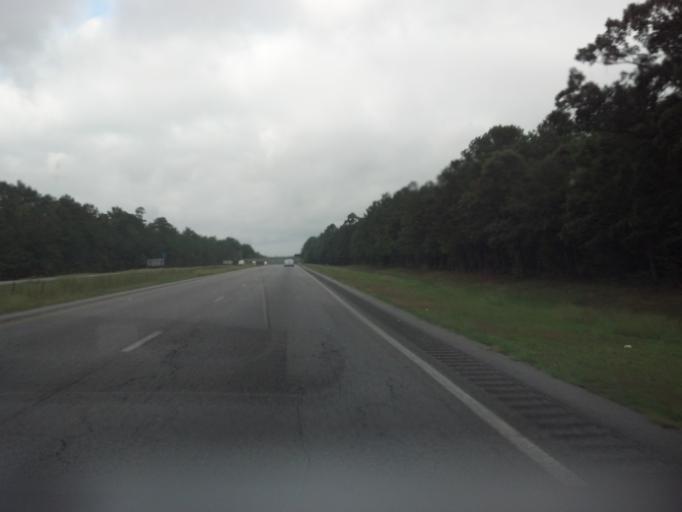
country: US
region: North Carolina
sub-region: Nash County
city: Rocky Mount
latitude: 35.9312
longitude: -77.7017
